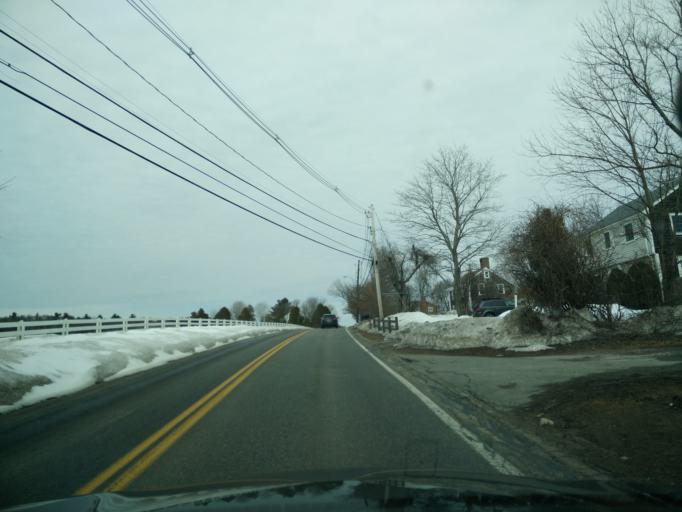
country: US
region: Massachusetts
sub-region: Norfolk County
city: Westwood
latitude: 42.1949
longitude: -71.2496
